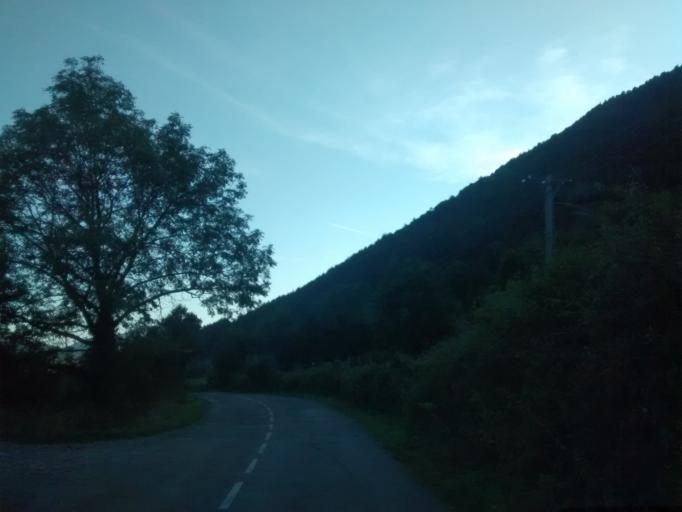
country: ES
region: Aragon
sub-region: Provincia de Huesca
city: Anso
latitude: 42.7704
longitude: -0.7441
